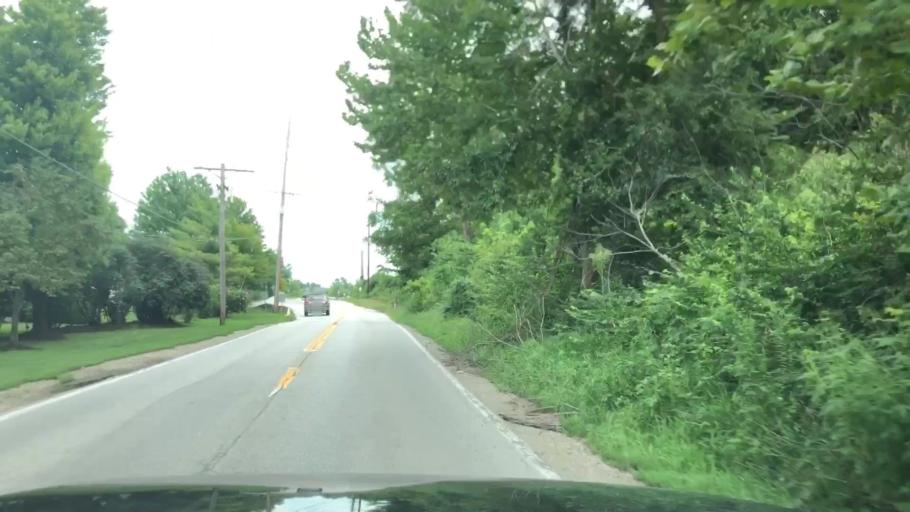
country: US
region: Missouri
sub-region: Saint Charles County
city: Saint Charles
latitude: 38.8152
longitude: -90.5235
